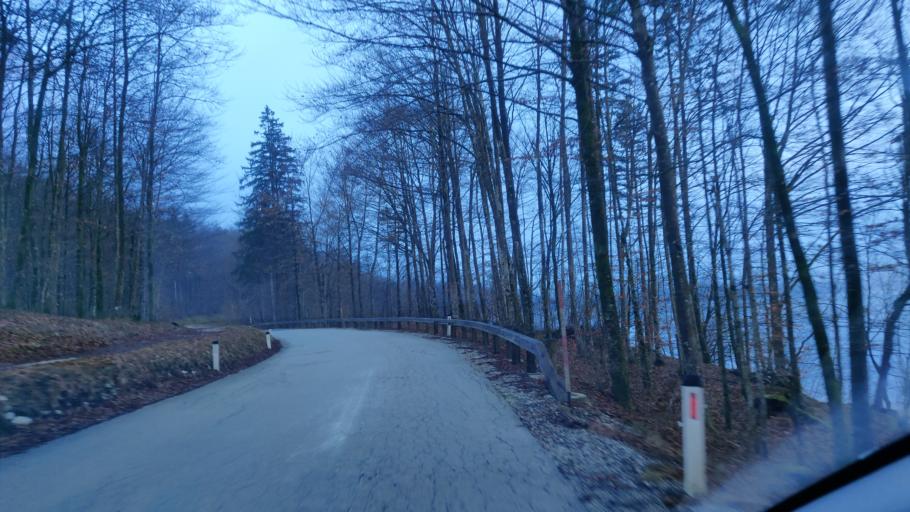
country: SI
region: Bohinj
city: Bohinjska Bistrica
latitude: 46.2810
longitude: 13.8469
